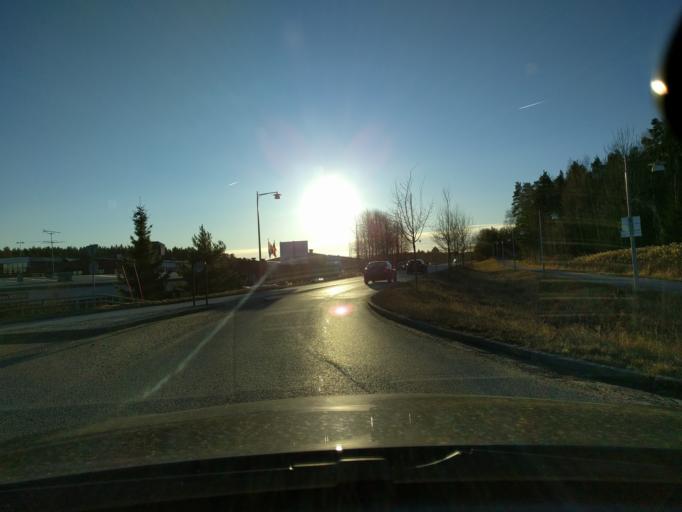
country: SE
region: Stockholm
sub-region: Taby Kommun
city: Taby
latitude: 59.4835
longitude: 18.0549
